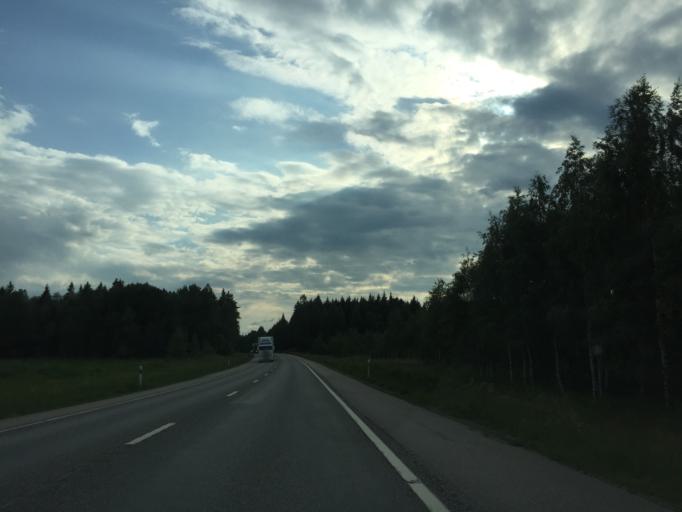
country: SE
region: OErebro
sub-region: Lindesbergs Kommun
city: Fellingsbro
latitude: 59.3496
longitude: 15.6420
